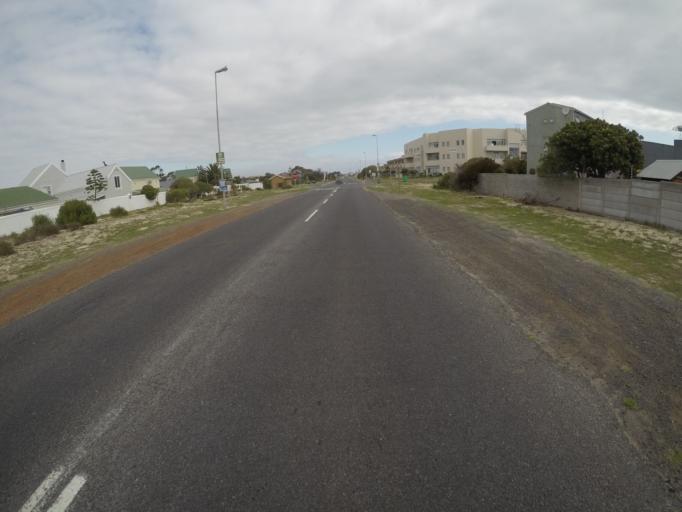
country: ZA
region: Western Cape
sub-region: City of Cape Town
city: Atlantis
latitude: -33.7105
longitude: 18.4467
